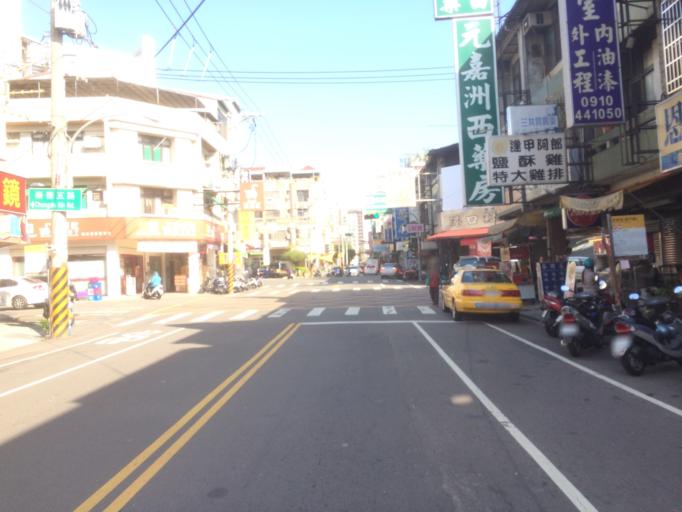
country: TW
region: Taiwan
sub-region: Taichung City
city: Taichung
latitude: 24.1786
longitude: 120.6907
